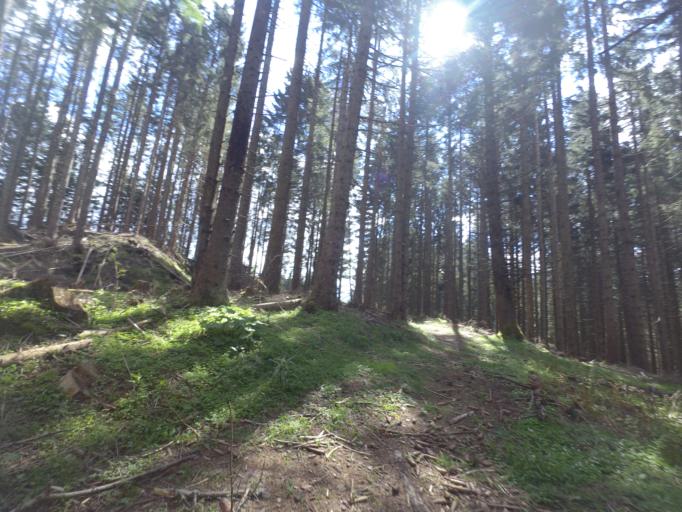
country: AT
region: Salzburg
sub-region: Politischer Bezirk Zell am See
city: Lend
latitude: 47.3086
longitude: 13.0597
